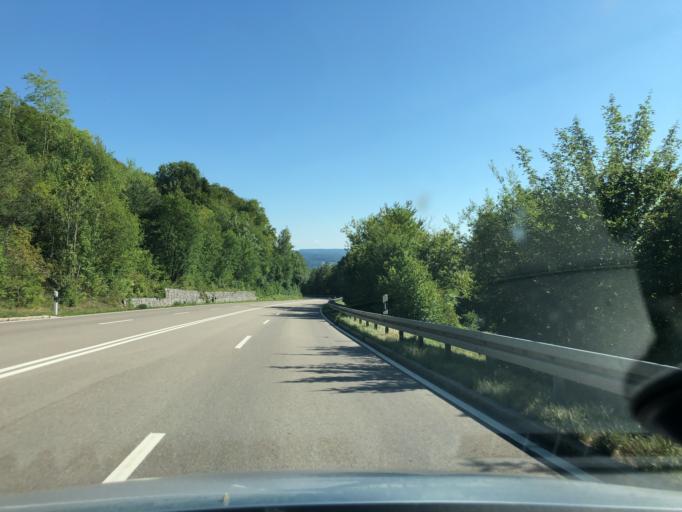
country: DE
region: Baden-Wuerttemberg
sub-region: Freiburg Region
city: Dogern
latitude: 47.6310
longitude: 8.1842
